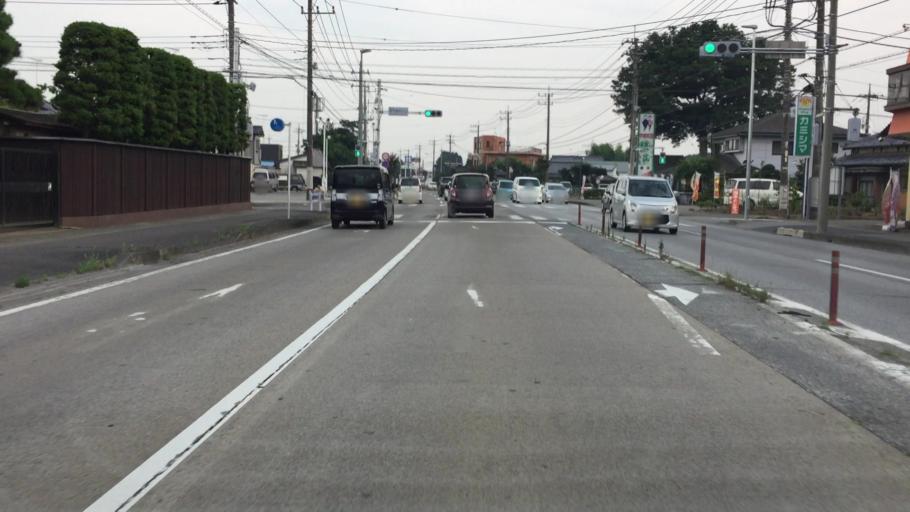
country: JP
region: Tochigi
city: Tochigi
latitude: 36.3725
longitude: 139.7153
